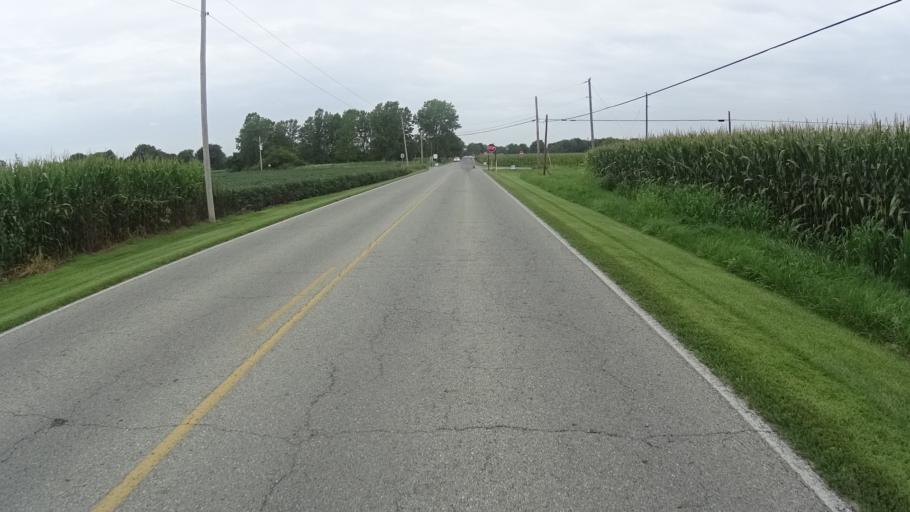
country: US
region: Indiana
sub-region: Madison County
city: Lapel
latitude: 40.0597
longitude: -85.8371
